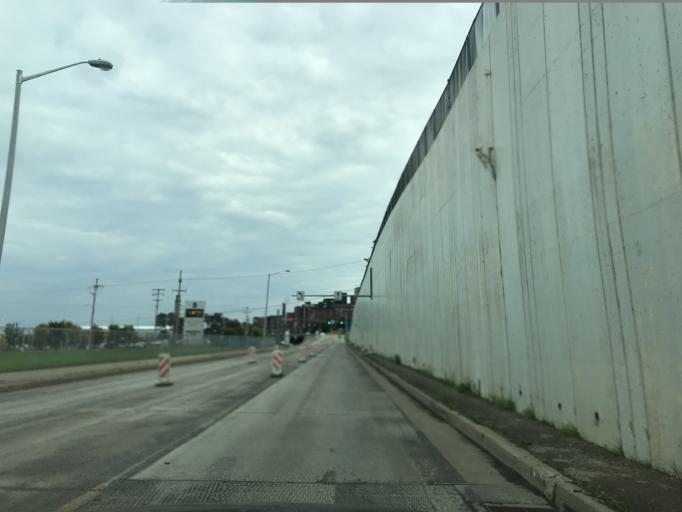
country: US
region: Pennsylvania
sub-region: Erie County
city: Erie
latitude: 42.1329
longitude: -80.0942
